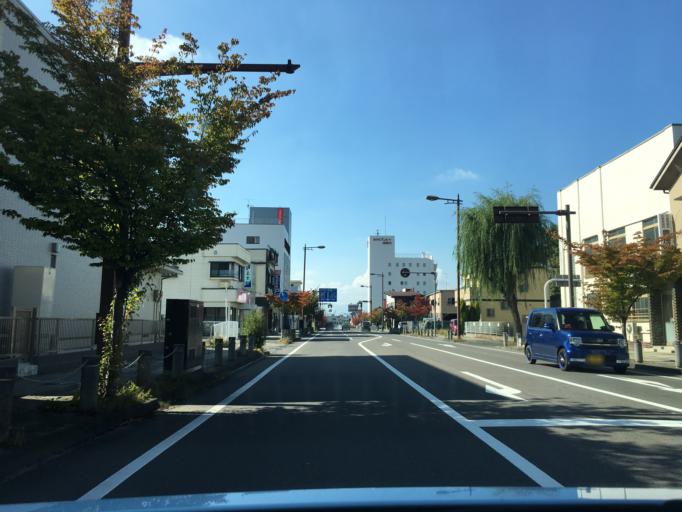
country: JP
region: Fukushima
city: Sukagawa
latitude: 37.2869
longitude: 140.3771
